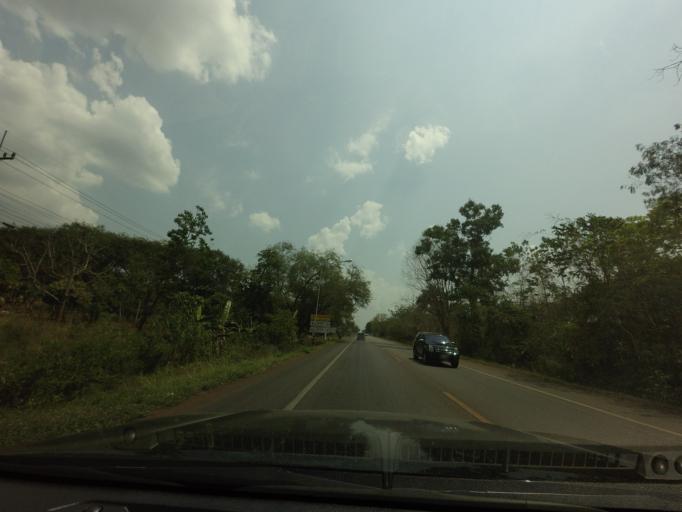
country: TH
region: Kanchanaburi
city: Sai Yok
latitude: 14.1332
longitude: 99.1578
